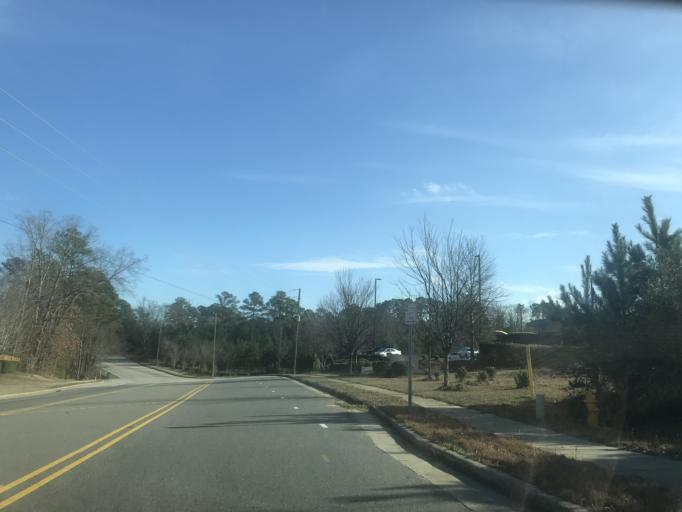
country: US
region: North Carolina
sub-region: Wake County
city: Garner
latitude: 35.7246
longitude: -78.5472
